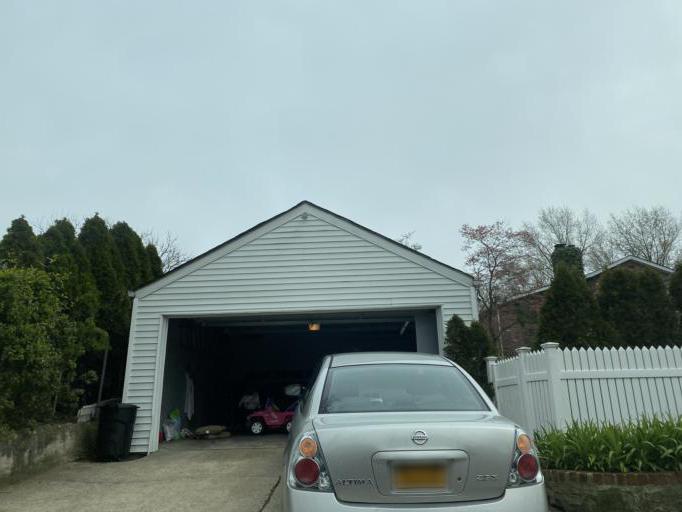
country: US
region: New York
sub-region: Nassau County
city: Bellerose
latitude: 40.7235
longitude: -73.7102
